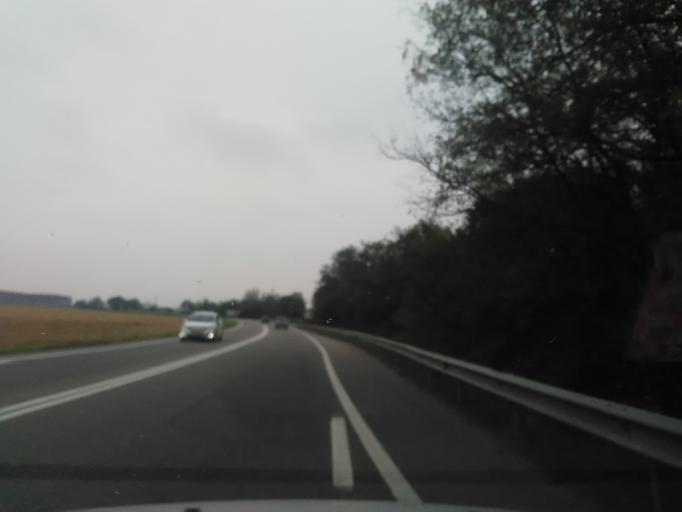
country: IT
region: Piedmont
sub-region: Provincia di Vercelli
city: Vercelli
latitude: 45.3071
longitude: 8.4029
